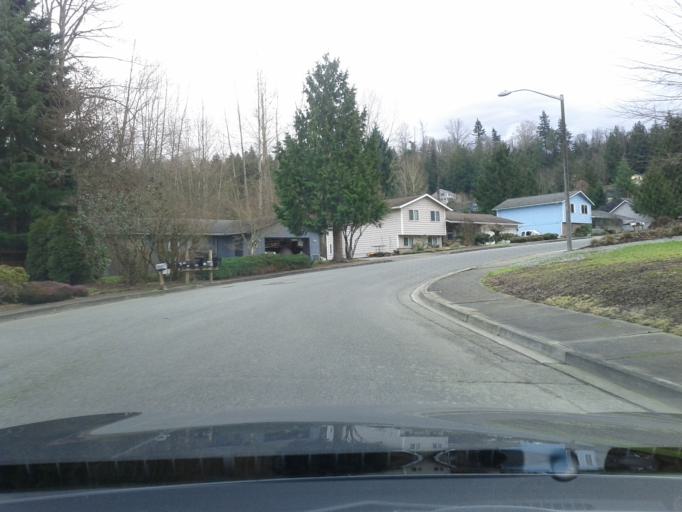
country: US
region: Washington
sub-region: Skagit County
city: Mount Vernon
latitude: 48.4329
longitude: -122.2861
